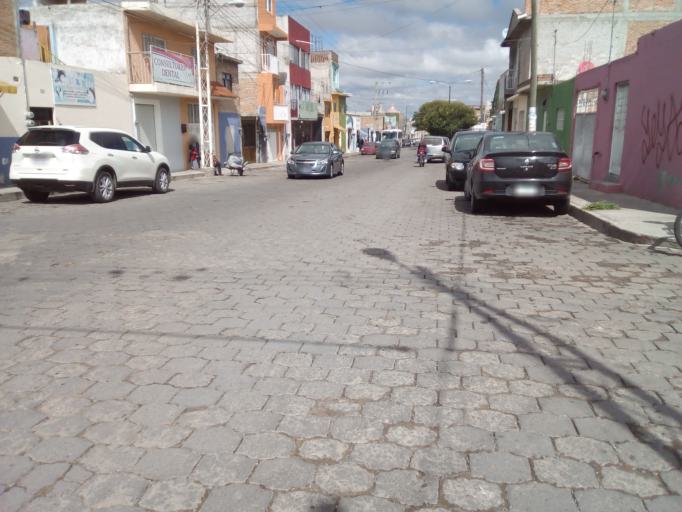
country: MX
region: Guerrero
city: San Luis de la Paz
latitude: 21.2950
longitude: -100.5115
